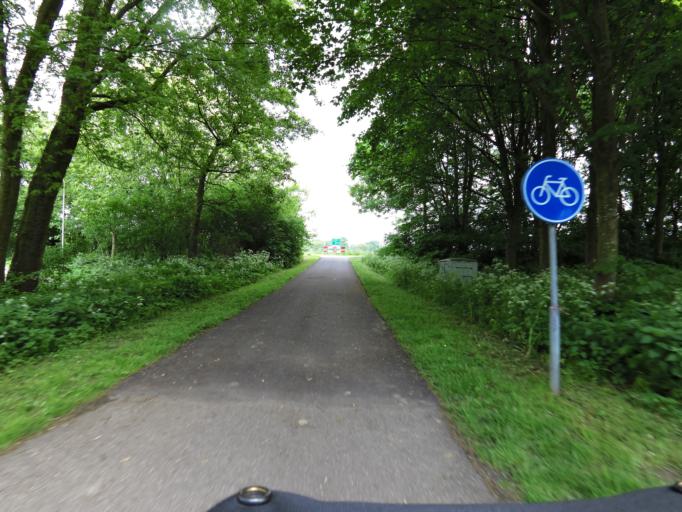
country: NL
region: South Holland
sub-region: Gemeente Maassluis
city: Maassluis
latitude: 51.8527
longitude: 4.2481
